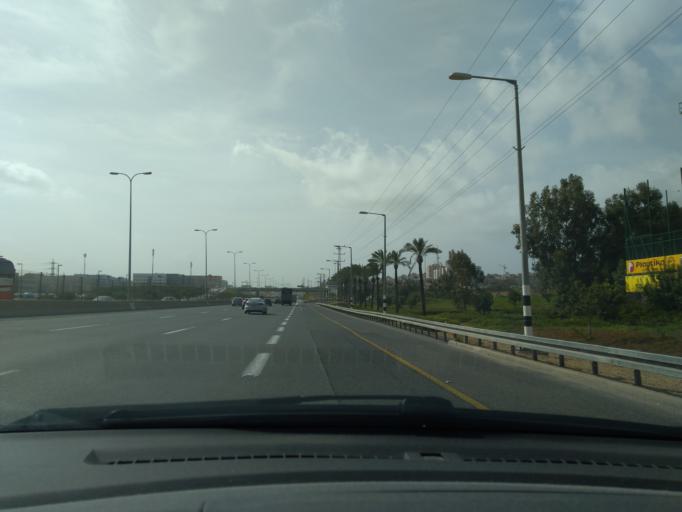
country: IL
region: Central District
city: Even Yehuda
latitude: 32.2911
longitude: 34.8605
